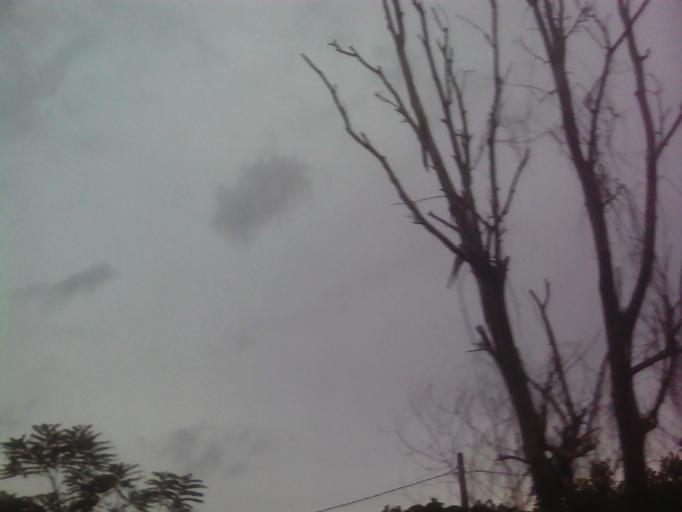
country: MY
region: Penang
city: Perai
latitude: 5.4057
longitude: 100.3905
